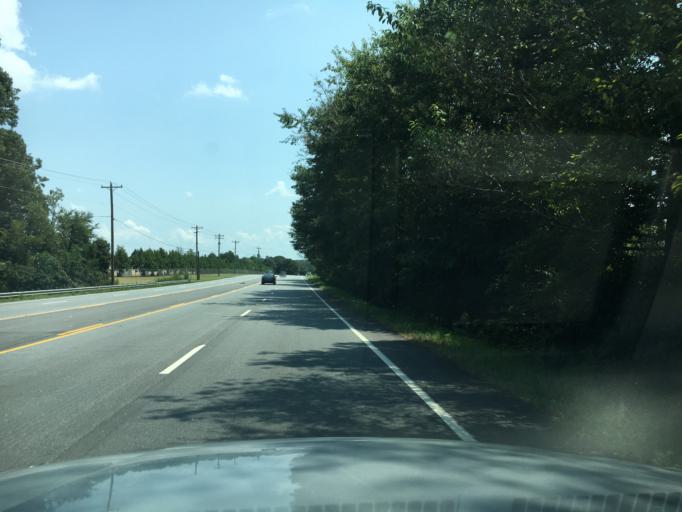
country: US
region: South Carolina
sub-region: Anderson County
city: Pendleton
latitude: 34.6140
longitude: -82.7707
